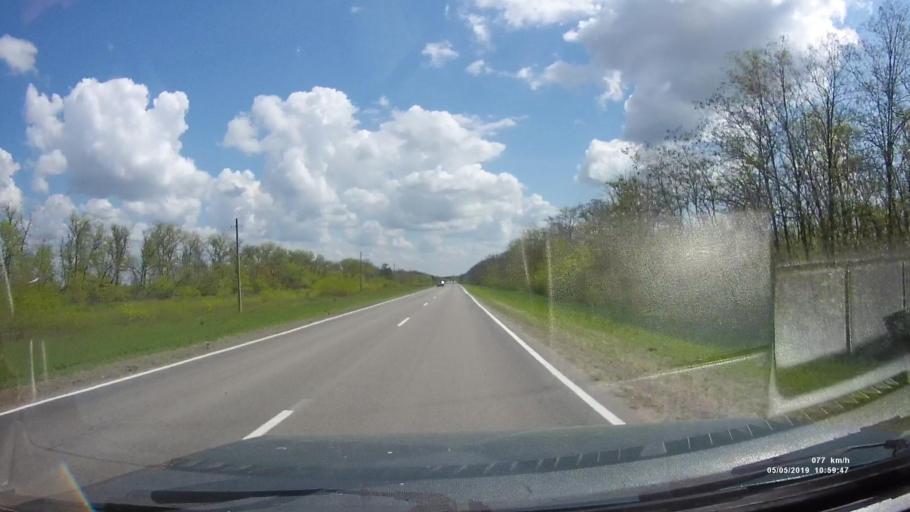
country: RU
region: Rostov
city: Ust'-Donetskiy
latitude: 47.6716
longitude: 40.8745
